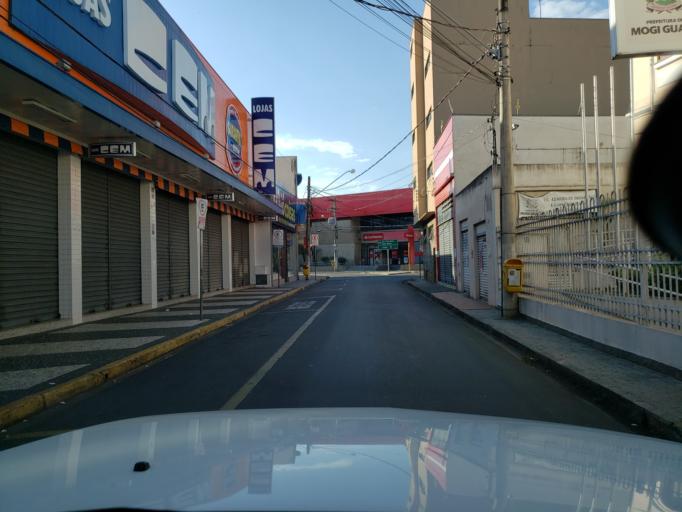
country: BR
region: Sao Paulo
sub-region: Moji-Guacu
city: Mogi-Gaucu
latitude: -22.3718
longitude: -46.9429
